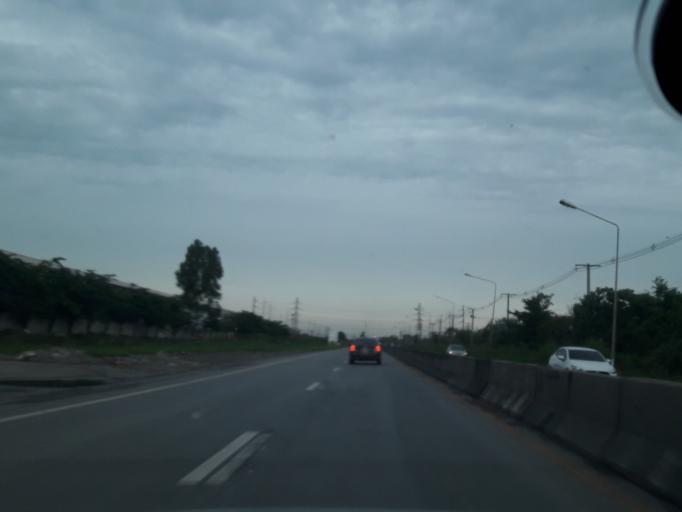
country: TH
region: Pathum Thani
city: Ban Rangsit
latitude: 14.0353
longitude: 100.7490
